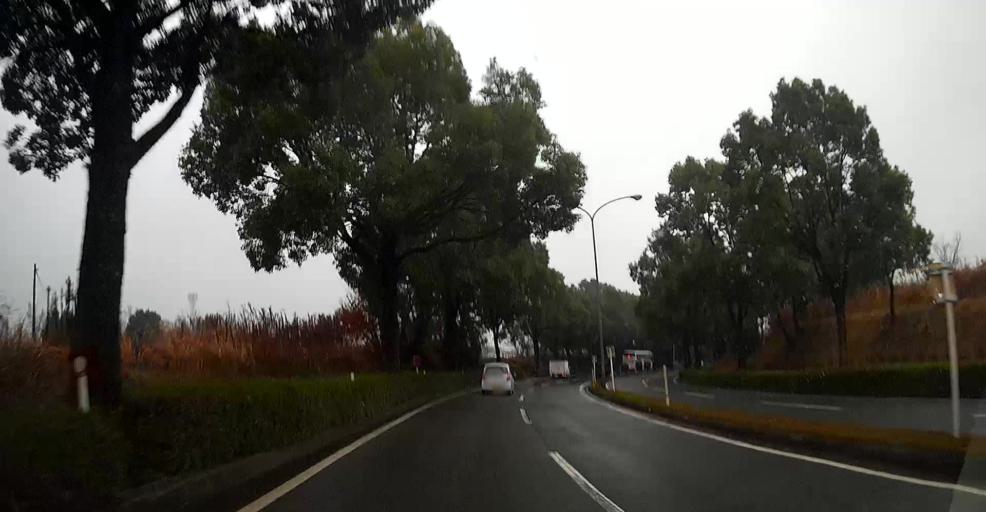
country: JP
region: Kumamoto
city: Ozu
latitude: 32.8260
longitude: 130.8594
